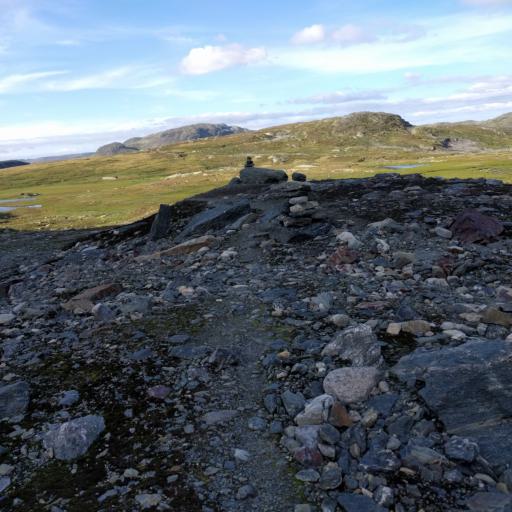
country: NO
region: Aust-Agder
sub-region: Bykle
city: Hovden
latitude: 59.9290
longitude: 7.2162
